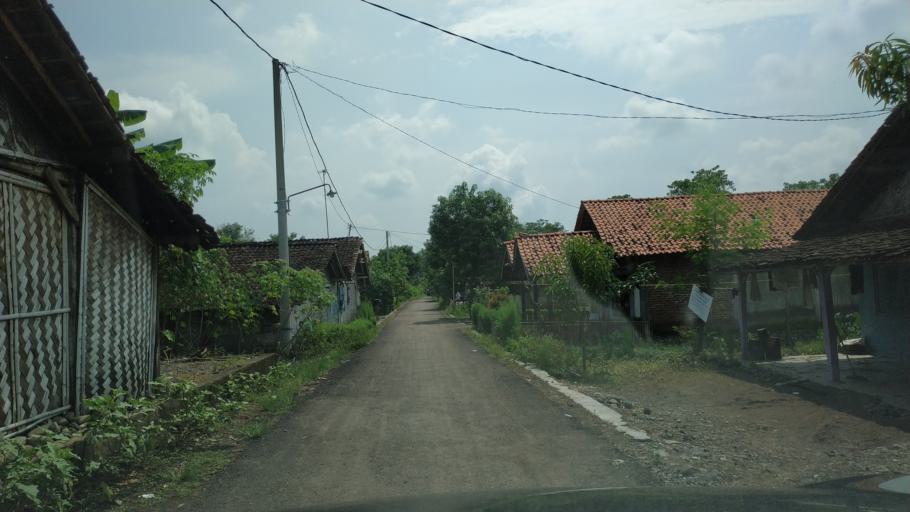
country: ID
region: Central Java
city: Margasari
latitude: -7.0937
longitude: 108.9750
